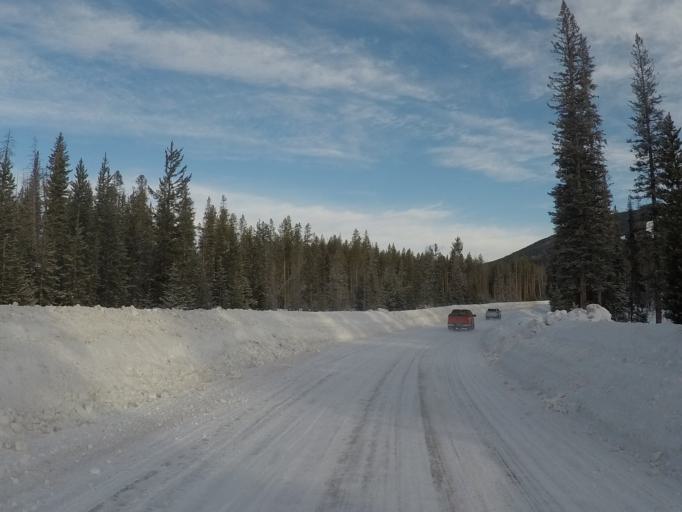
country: US
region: Montana
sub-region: Granite County
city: Philipsburg
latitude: 46.2328
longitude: -113.2465
